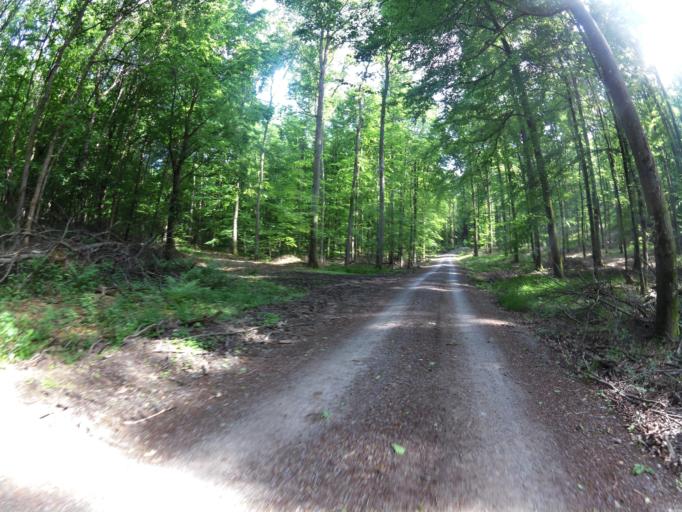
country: DE
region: Bavaria
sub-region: Regierungsbezirk Unterfranken
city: Uettingen
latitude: 49.7786
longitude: 9.7416
